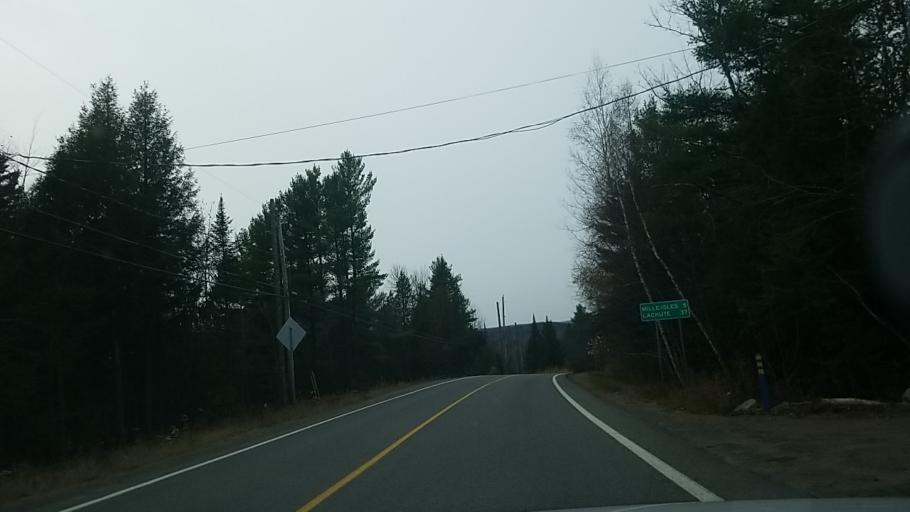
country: CA
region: Quebec
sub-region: Laurentides
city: Saint-Colomban
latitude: 45.7892
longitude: -74.1255
